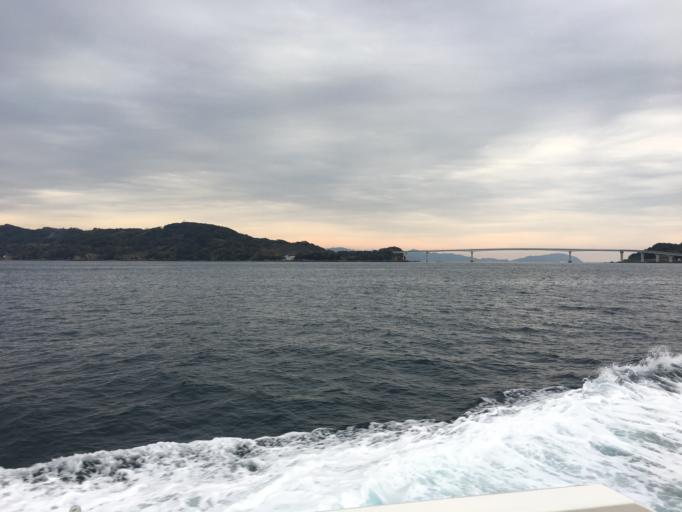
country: JP
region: Nagasaki
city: Nagasaki-shi
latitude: 32.7057
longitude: 129.7922
